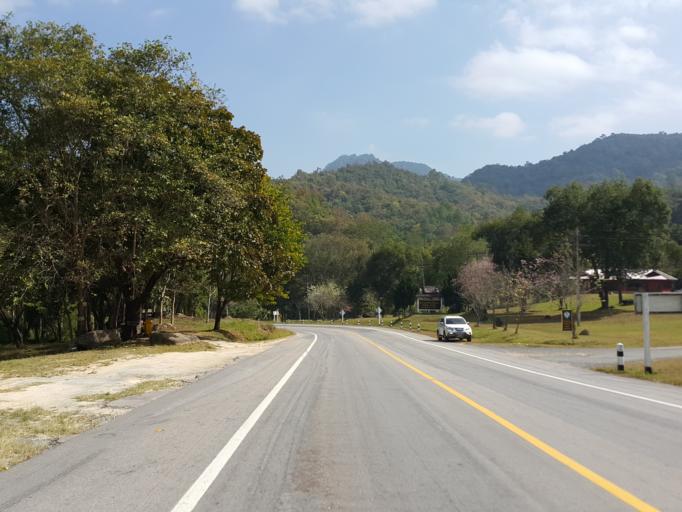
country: TH
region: Lampang
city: Wang Nuea
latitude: 19.0783
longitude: 99.3975
